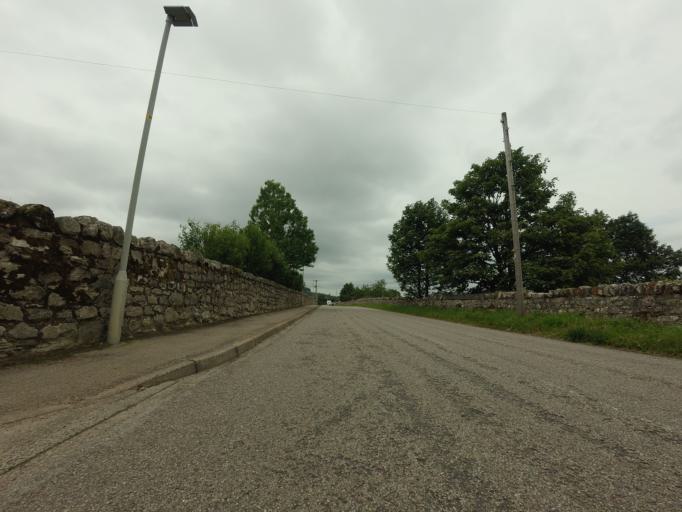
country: GB
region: Scotland
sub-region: Highland
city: Alness
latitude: 57.8838
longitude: -4.3653
